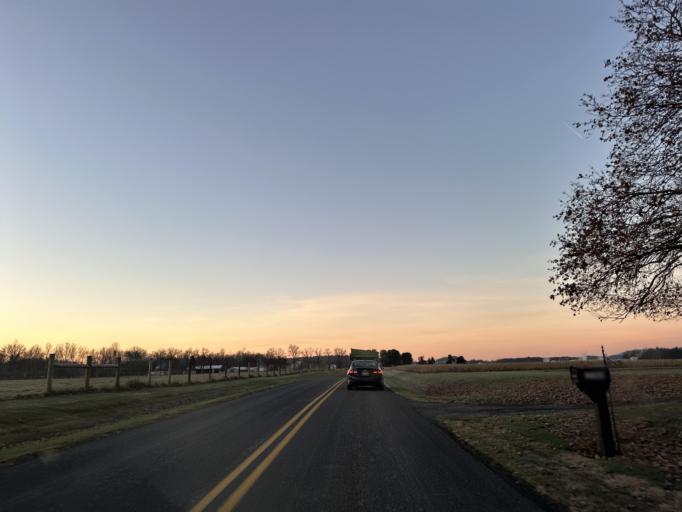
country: US
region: Virginia
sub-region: Rockingham County
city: Bridgewater
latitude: 38.3852
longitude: -79.0777
